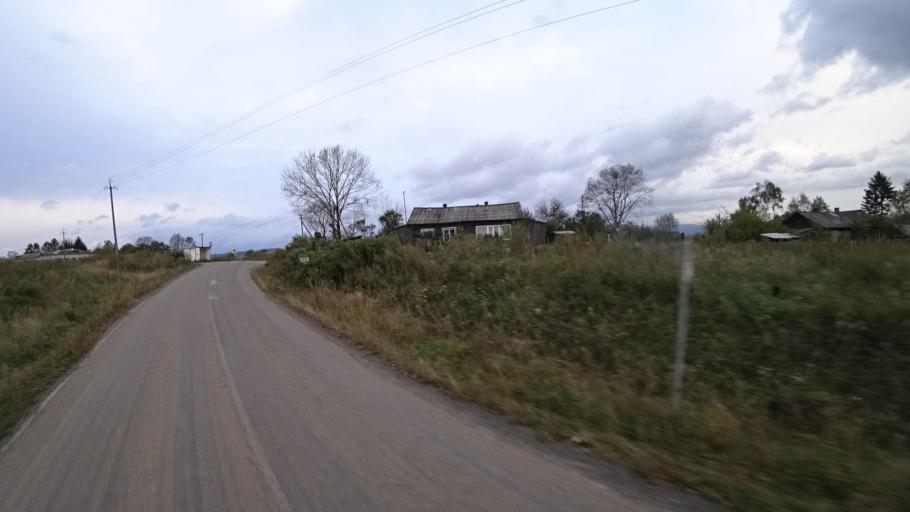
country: RU
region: Jewish Autonomous Oblast
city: Izvestkovyy
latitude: 48.9676
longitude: 131.5884
